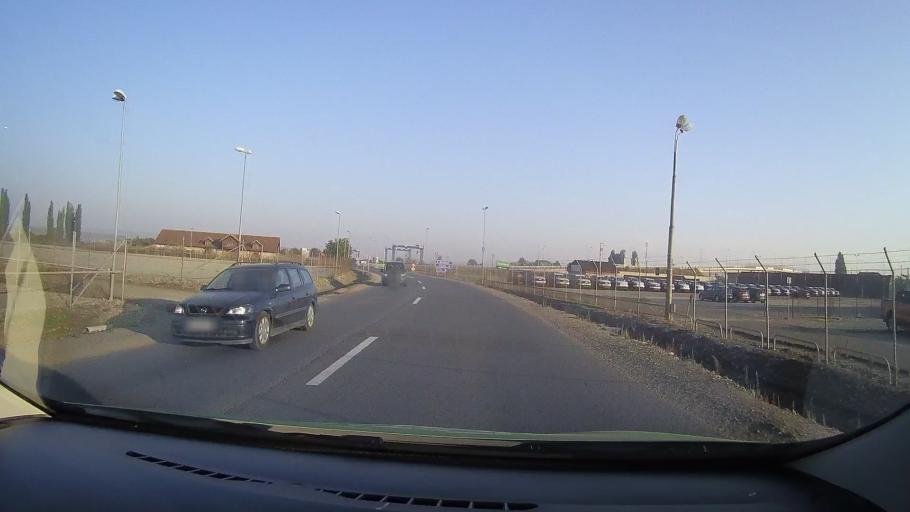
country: RO
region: Arad
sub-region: Comuna Curtici
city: Curtici
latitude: 46.3356
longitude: 21.2977
